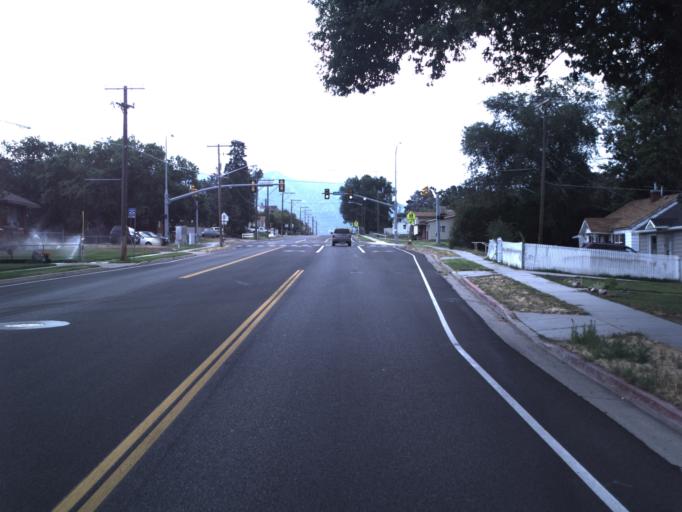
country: US
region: Utah
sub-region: Weber County
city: Roy
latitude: 41.1616
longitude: -112.0353
